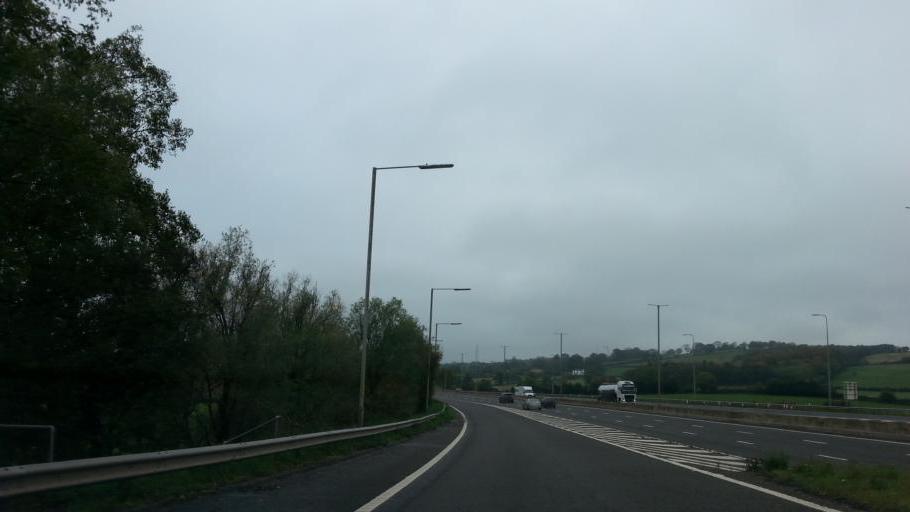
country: GB
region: England
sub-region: Worcestershire
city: Barnt Green
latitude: 52.3811
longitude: -2.0465
